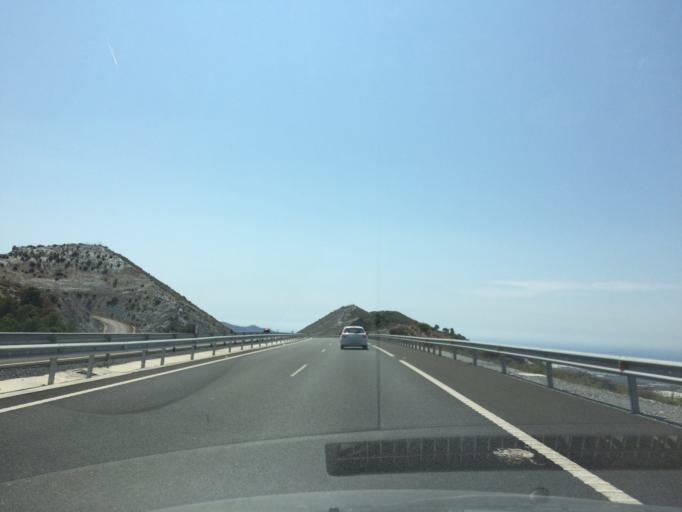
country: ES
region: Andalusia
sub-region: Provincia de Granada
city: Motril
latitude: 36.7638
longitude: -3.4851
